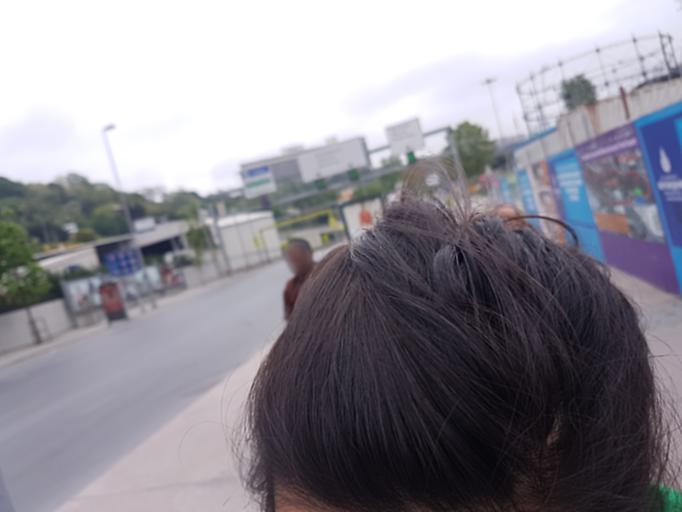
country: TR
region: Istanbul
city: Sisli
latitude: 41.0410
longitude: 28.9944
